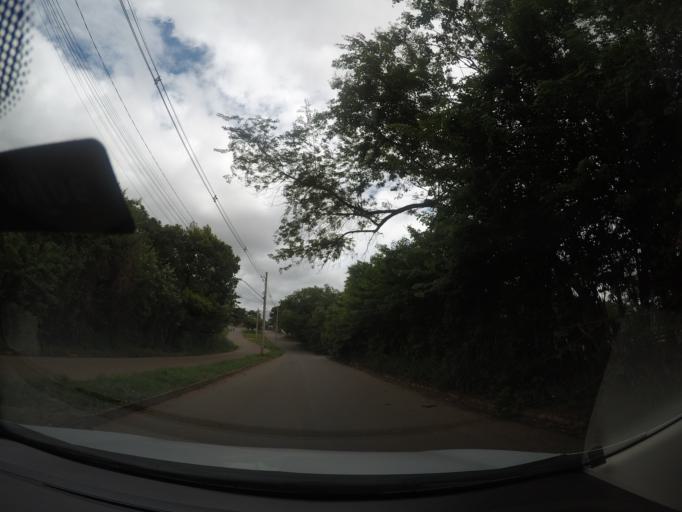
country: BR
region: Goias
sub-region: Goiania
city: Goiania
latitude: -16.7233
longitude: -49.3576
